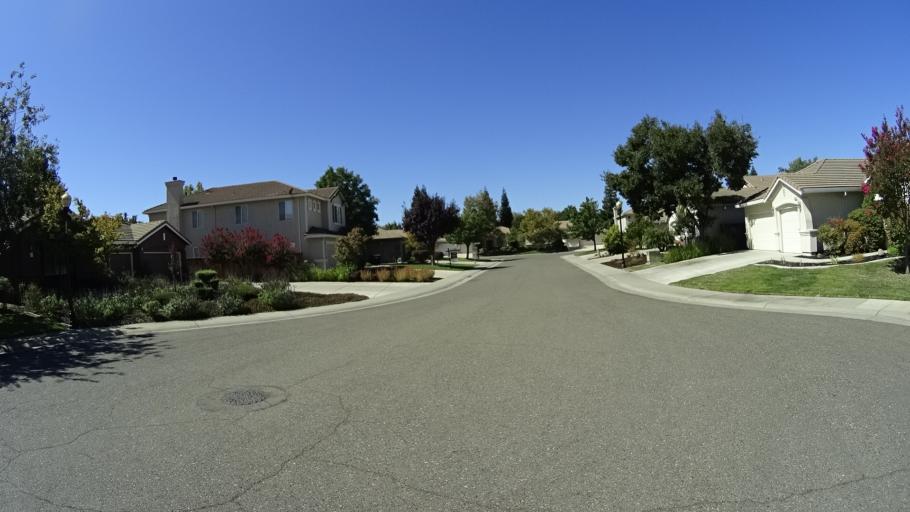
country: US
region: California
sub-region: Sacramento County
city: Laguna
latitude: 38.4145
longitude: -121.4675
